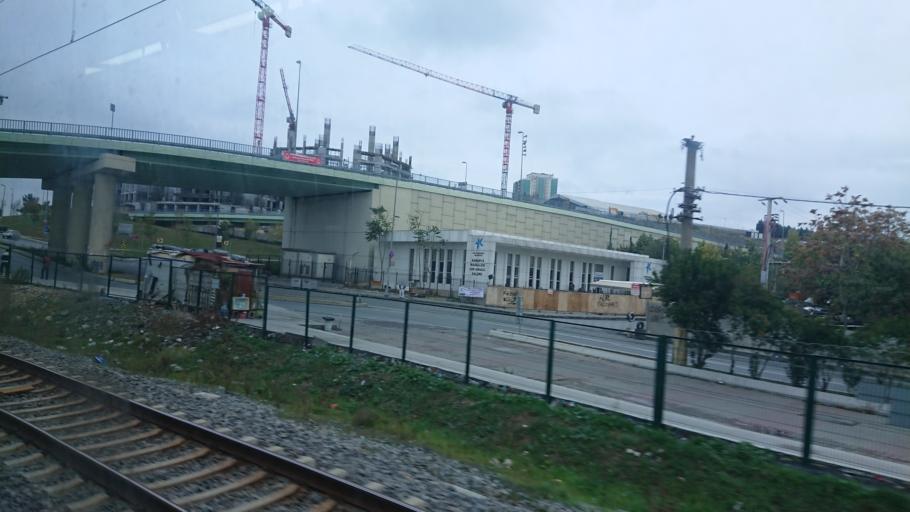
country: TR
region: Istanbul
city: Mahmutbey
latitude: 41.0114
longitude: 28.7720
